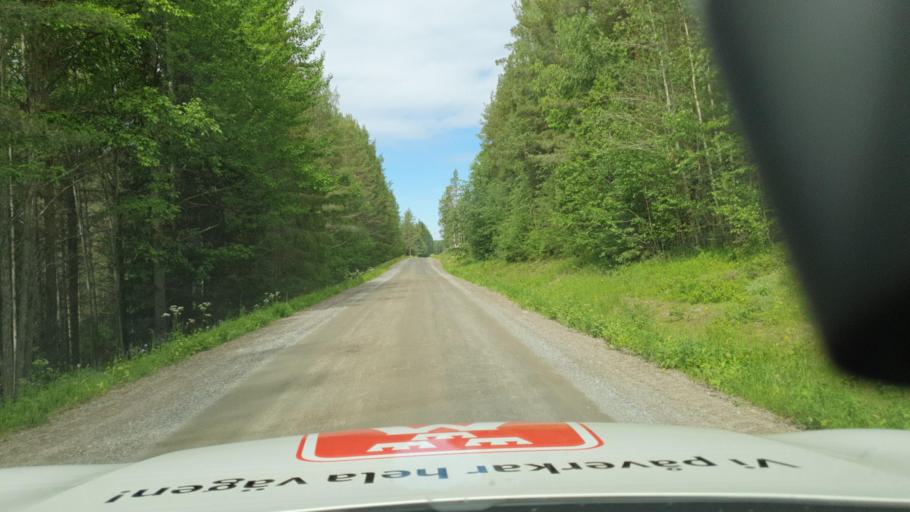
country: SE
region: Vaesterbotten
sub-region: Skelleftea Kommun
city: Burtraesk
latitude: 64.6203
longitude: 20.5674
